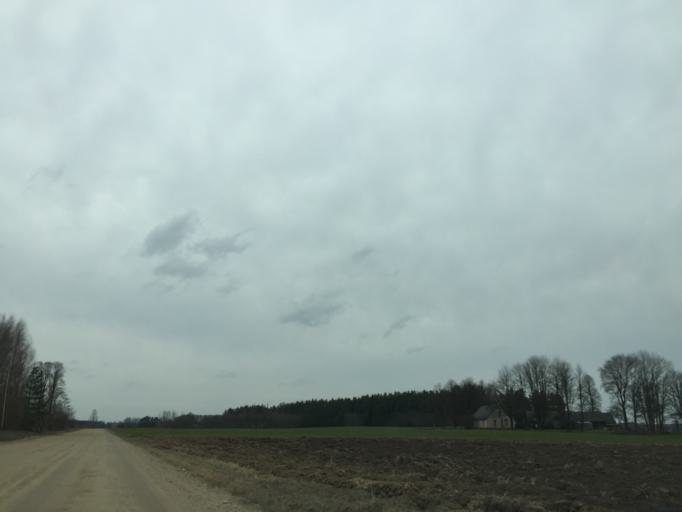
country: LV
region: Livani
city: Livani
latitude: 56.3096
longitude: 26.1647
